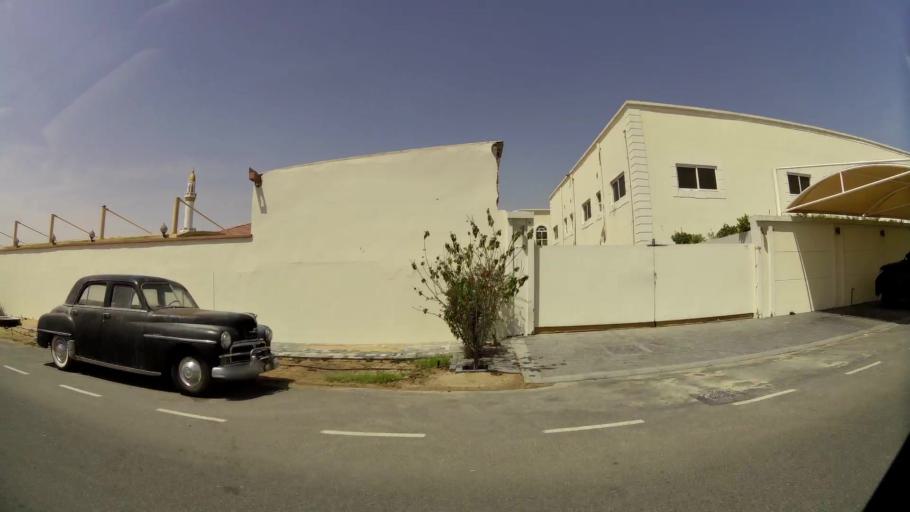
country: AE
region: Ash Shariqah
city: Sharjah
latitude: 25.1895
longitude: 55.4235
